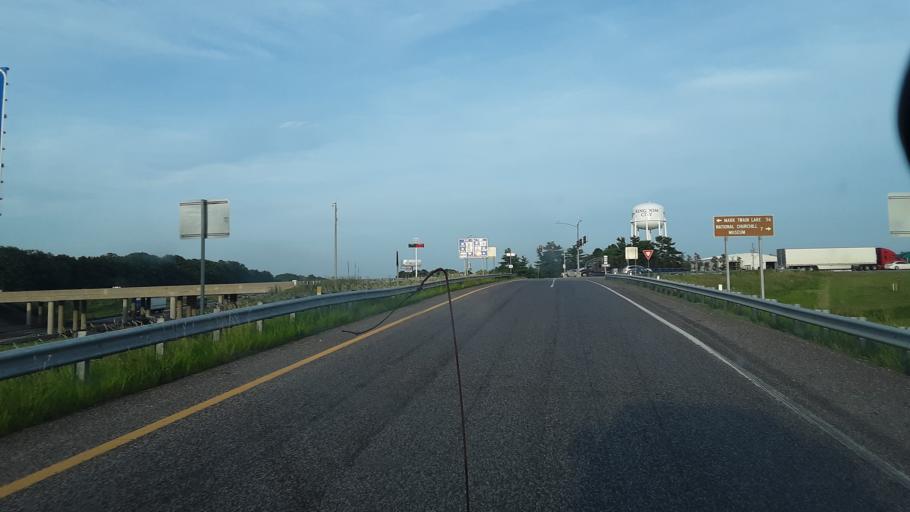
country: US
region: Missouri
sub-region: Callaway County
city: Fulton
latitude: 38.9439
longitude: -91.9427
